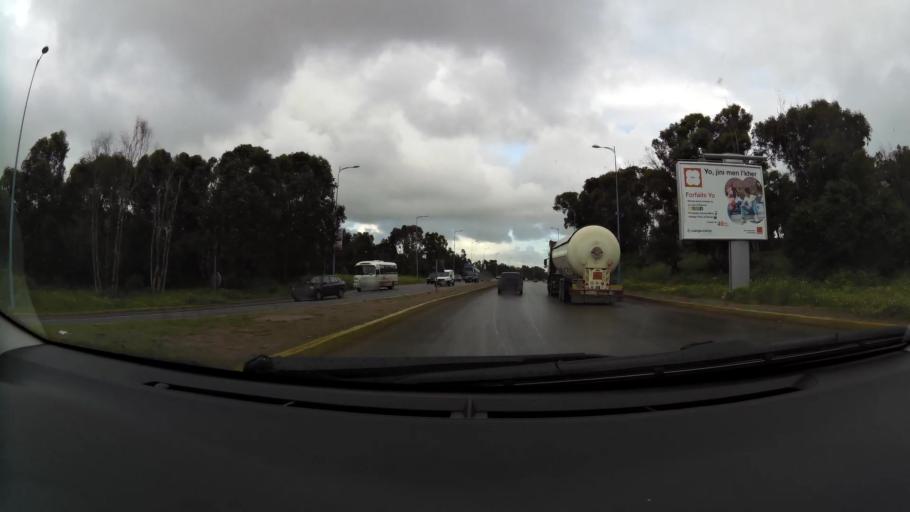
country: MA
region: Grand Casablanca
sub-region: Mohammedia
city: Mohammedia
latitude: 33.6777
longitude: -7.4116
